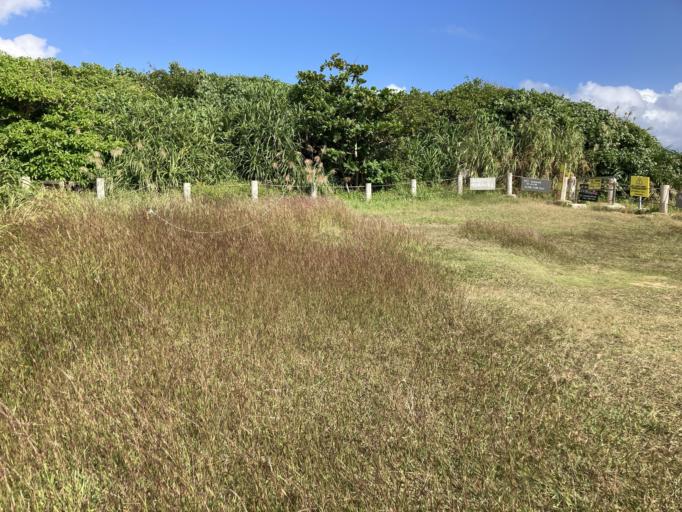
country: JP
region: Okinawa
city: Itoman
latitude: 26.0806
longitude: 127.6647
